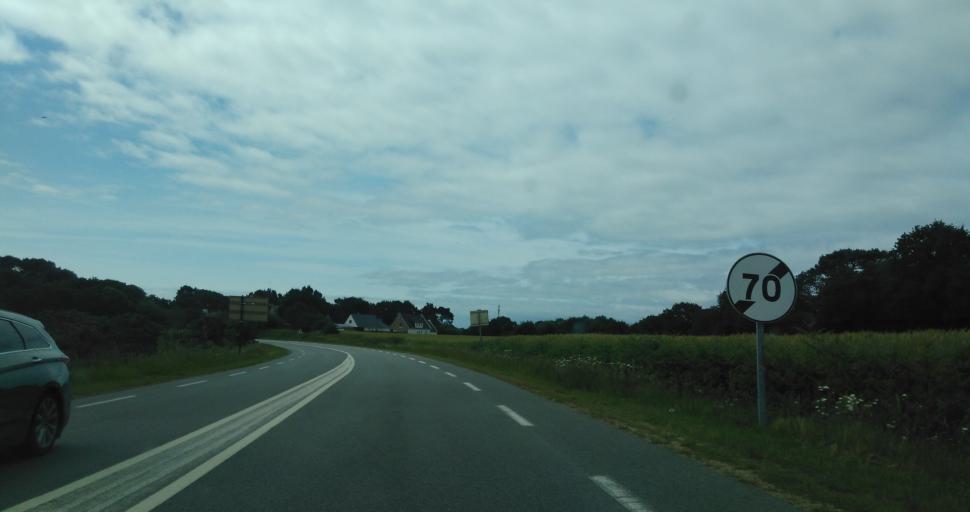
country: FR
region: Brittany
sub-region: Departement du Morbihan
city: La Trinite-sur-Mer
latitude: 47.6021
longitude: -3.0436
